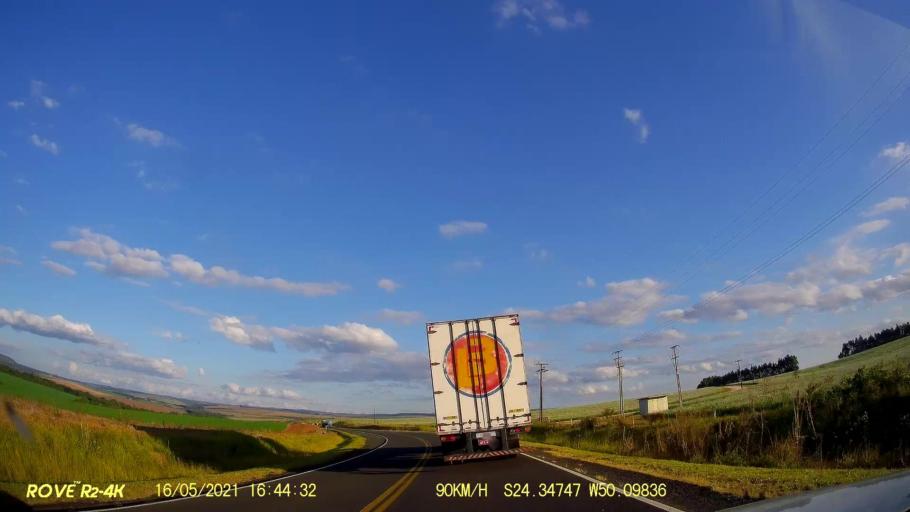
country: BR
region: Parana
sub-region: Pirai Do Sul
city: Pirai do Sul
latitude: -24.3476
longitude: -50.0985
